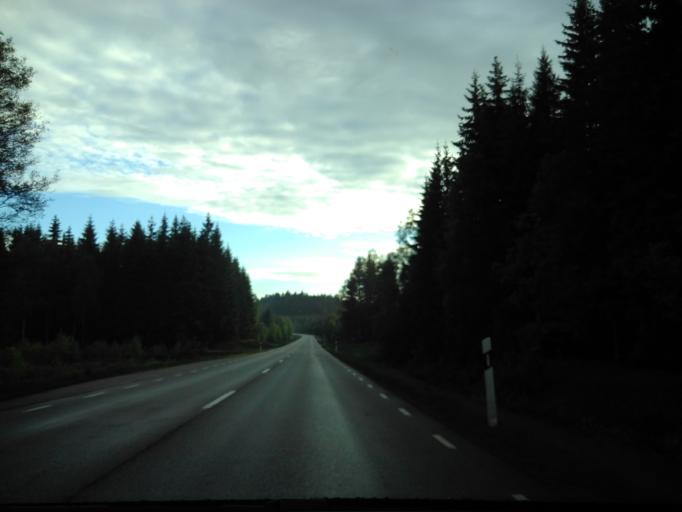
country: SE
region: Vaestra Goetaland
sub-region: Herrljunga Kommun
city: Herrljunga
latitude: 58.0904
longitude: 13.1274
